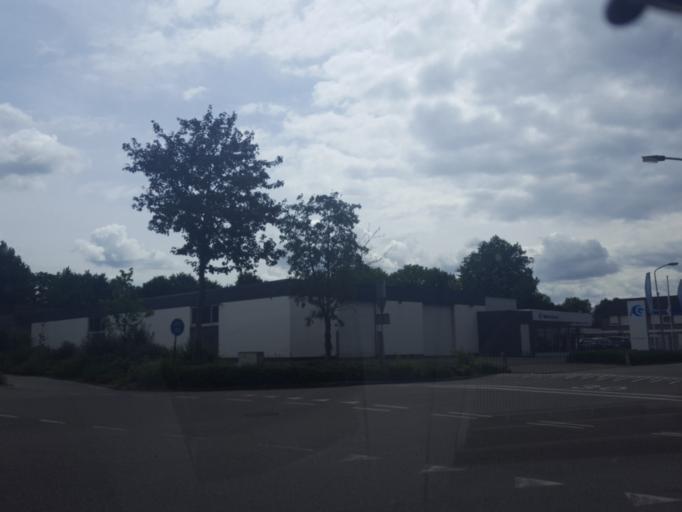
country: NL
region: Limburg
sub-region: Gemeente Weert
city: Weert
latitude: 51.2590
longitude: 5.6895
